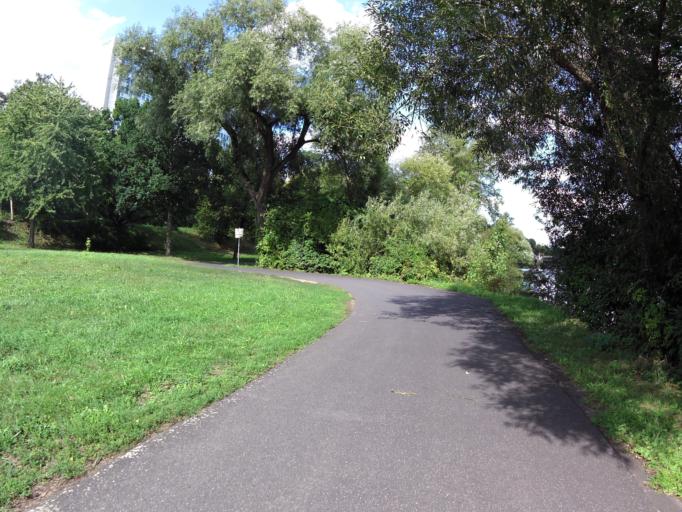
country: DE
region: Bavaria
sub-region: Regierungsbezirk Unterfranken
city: Schweinfurt
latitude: 50.0376
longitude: 10.2244
